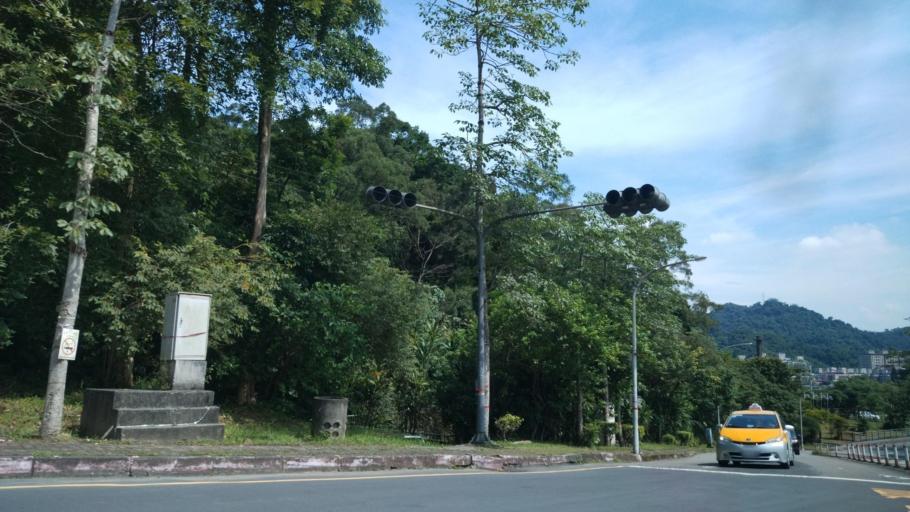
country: TW
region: Taipei
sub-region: Taipei
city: Banqiao
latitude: 24.9532
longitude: 121.5091
